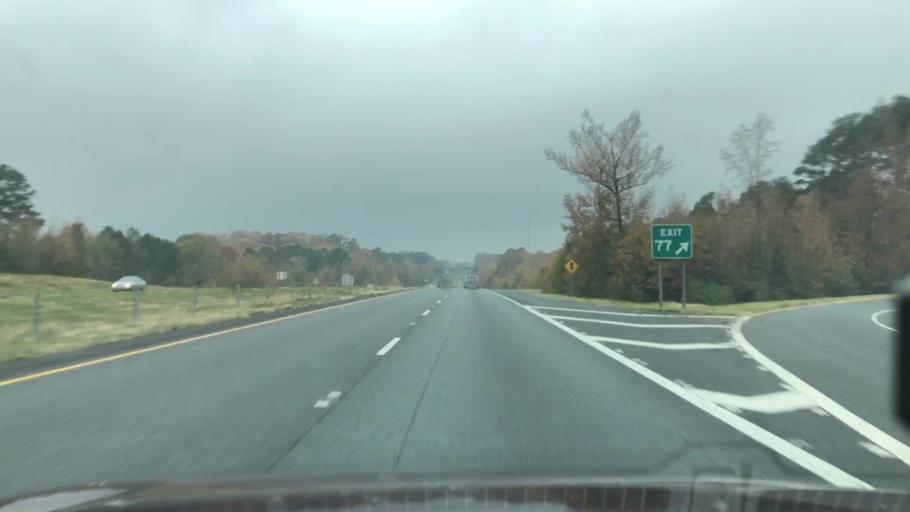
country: US
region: Louisiana
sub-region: Lincoln Parish
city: Grambling
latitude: 32.5485
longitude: -92.7882
